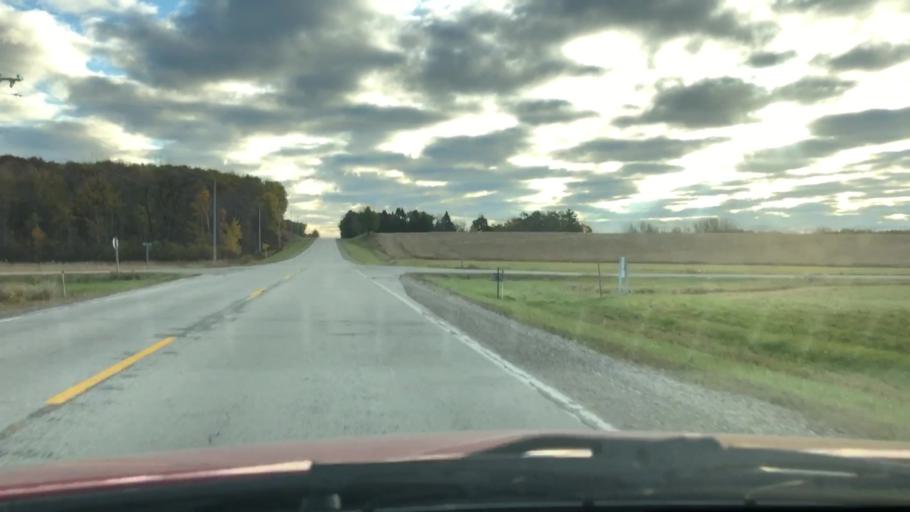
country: US
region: Wisconsin
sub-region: Outagamie County
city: Seymour
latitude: 44.4440
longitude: -88.2719
